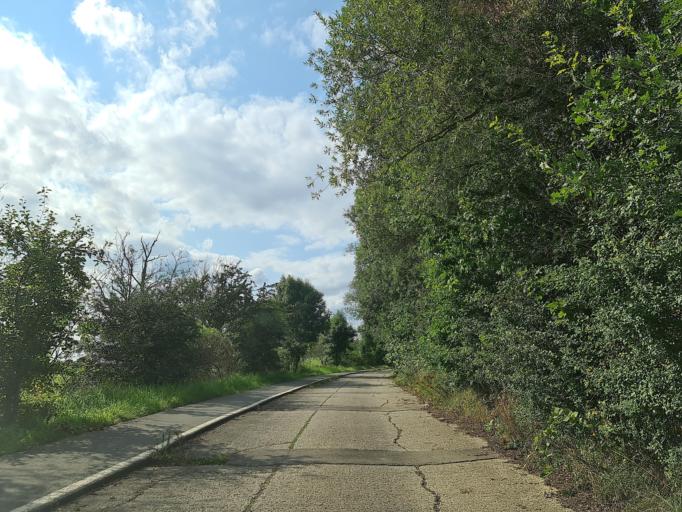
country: DE
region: Saxony
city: Syrau
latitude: 50.4985
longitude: 12.0775
